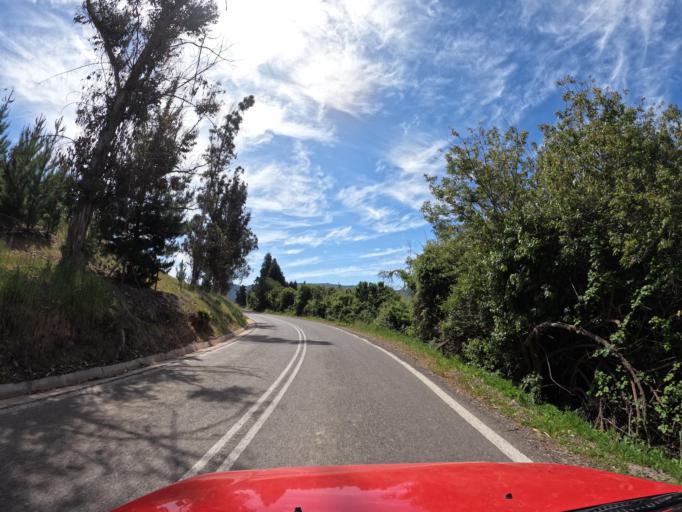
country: CL
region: Maule
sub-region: Provincia de Talca
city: Talca
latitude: -35.0033
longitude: -71.9834
